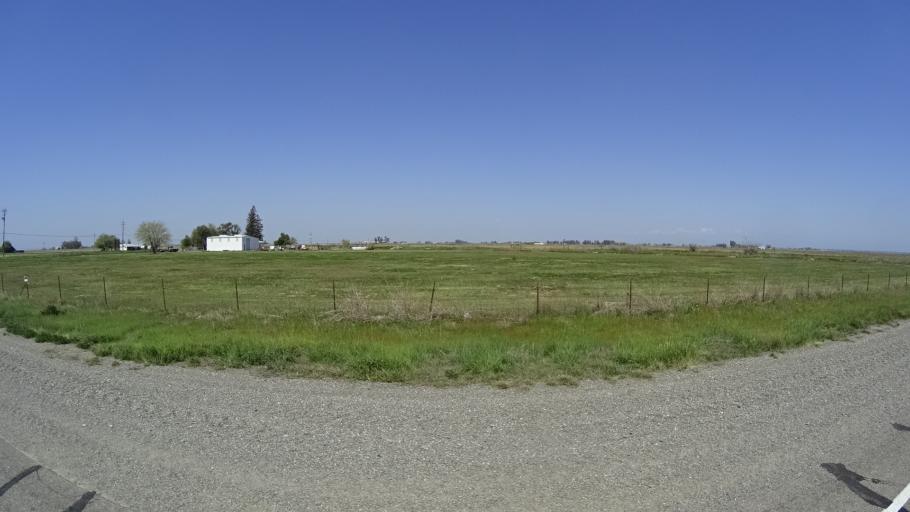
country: US
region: California
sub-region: Glenn County
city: Willows
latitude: 39.5218
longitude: -122.1106
